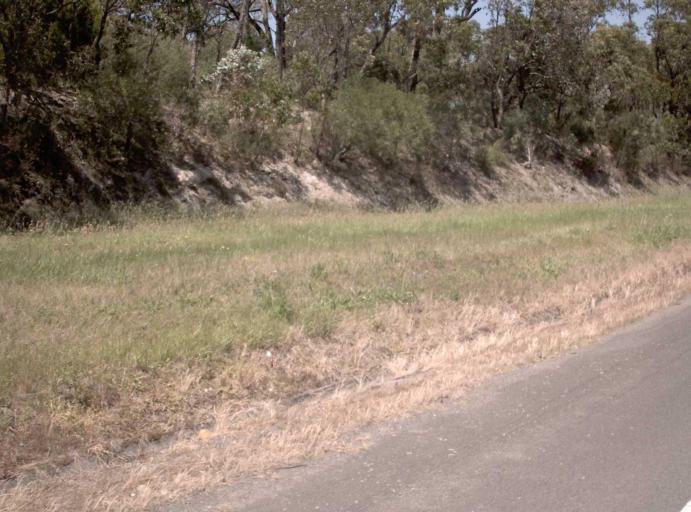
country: AU
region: Victoria
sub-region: Latrobe
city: Moe
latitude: -38.1915
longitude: 146.2843
